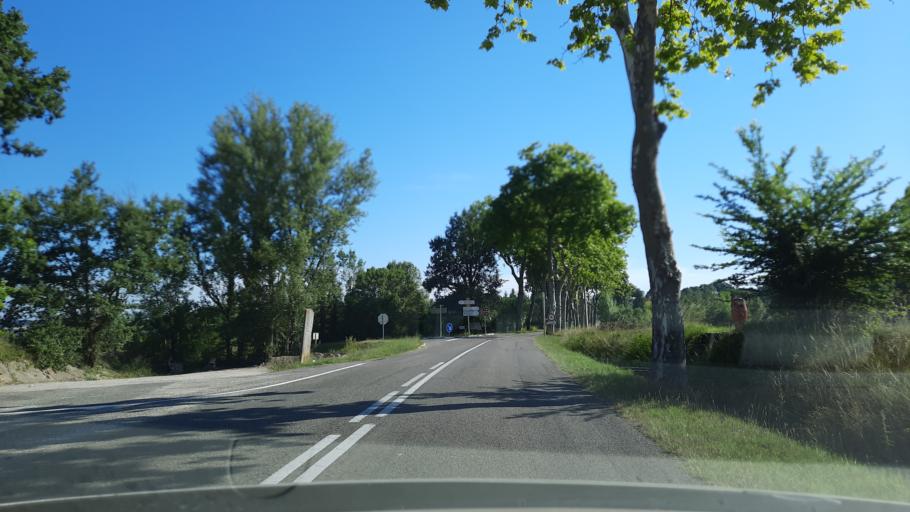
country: FR
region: Midi-Pyrenees
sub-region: Departement du Tarn-et-Garonne
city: Molieres
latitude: 44.1990
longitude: 1.3727
